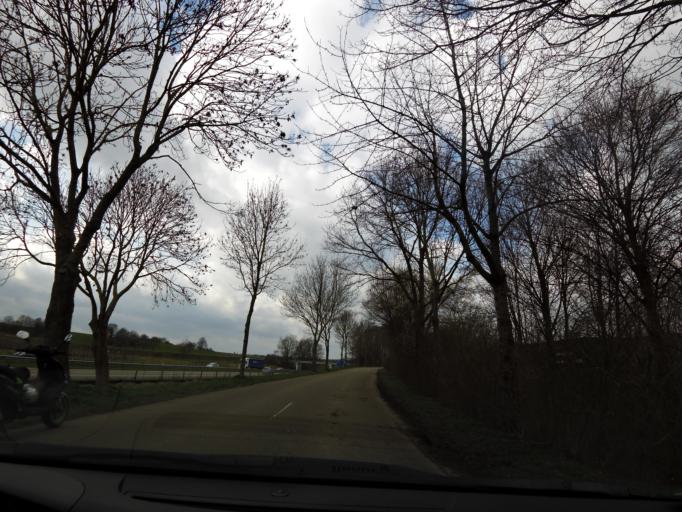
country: NL
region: Limburg
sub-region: Gemeente Voerendaal
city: Kunrade
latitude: 50.8732
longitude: 5.9231
